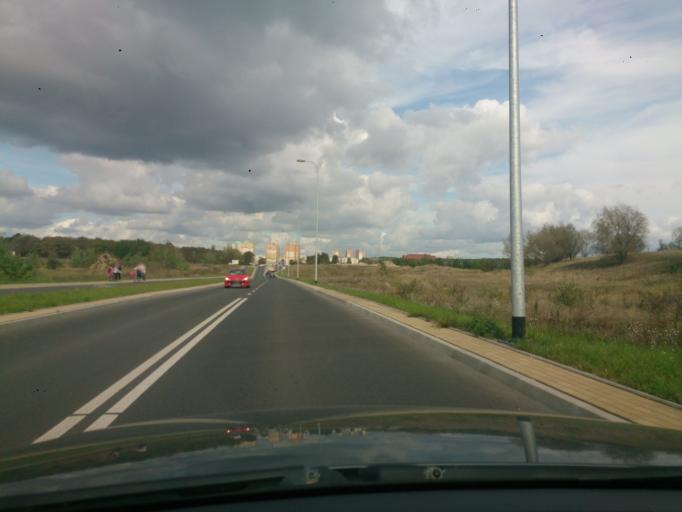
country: PL
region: Kujawsko-Pomorskie
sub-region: Grudziadz
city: Grudziadz
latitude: 53.4439
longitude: 18.7148
